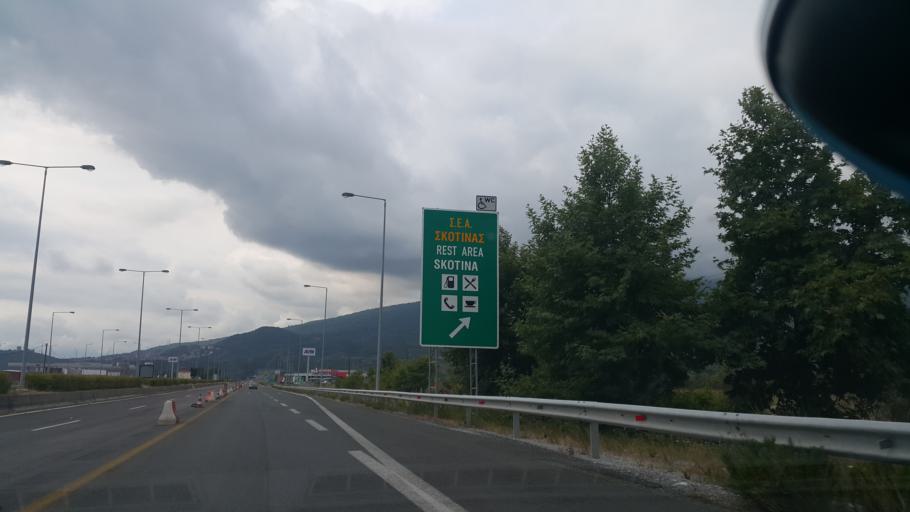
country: GR
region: Central Macedonia
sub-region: Nomos Pierias
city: Leptokarya
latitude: 40.0305
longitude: 22.5711
